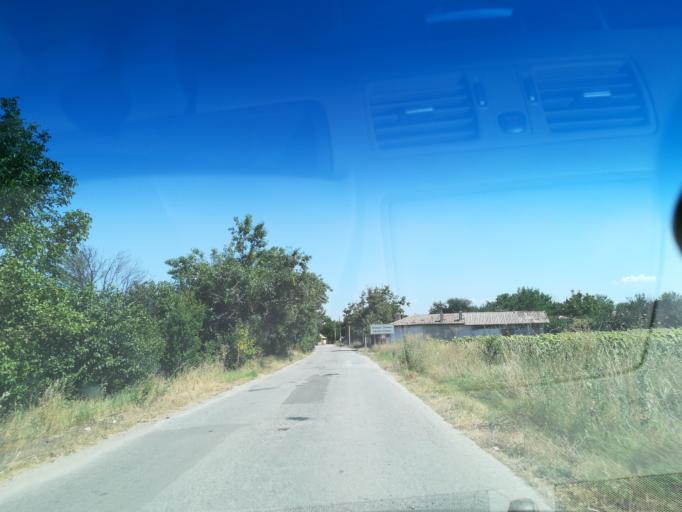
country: BG
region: Plovdiv
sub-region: Obshtina Sadovo
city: Sadovo
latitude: 42.0123
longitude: 25.0437
